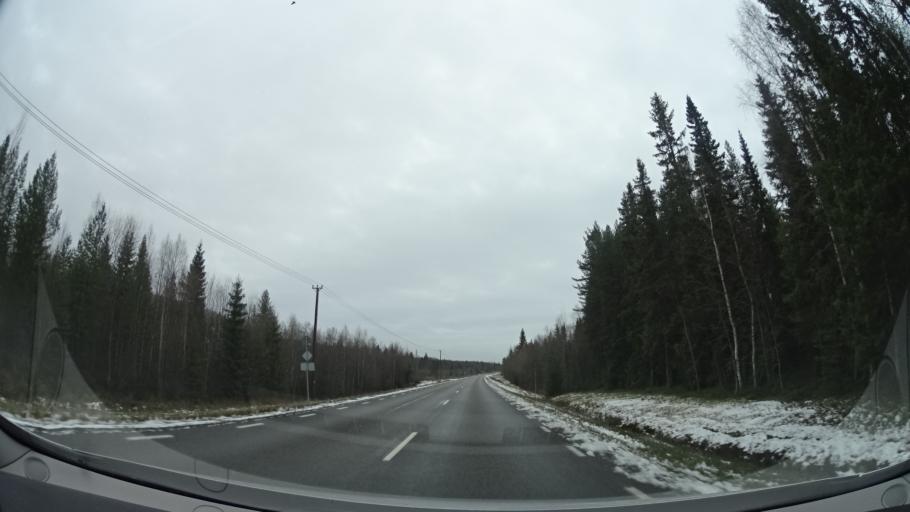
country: SE
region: Jaemtland
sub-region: Stroemsunds Kommun
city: Stroemsund
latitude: 63.9218
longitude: 15.5144
